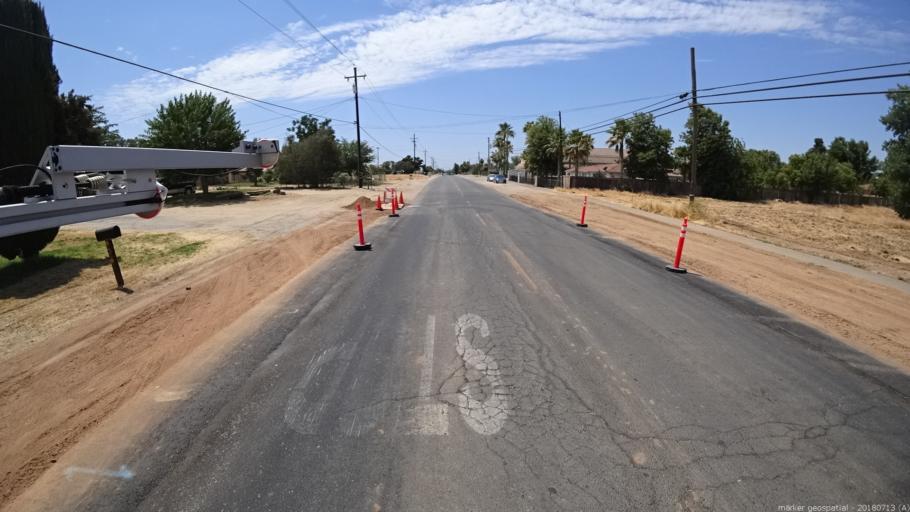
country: US
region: California
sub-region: Madera County
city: Madera
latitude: 36.9858
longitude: -120.0632
